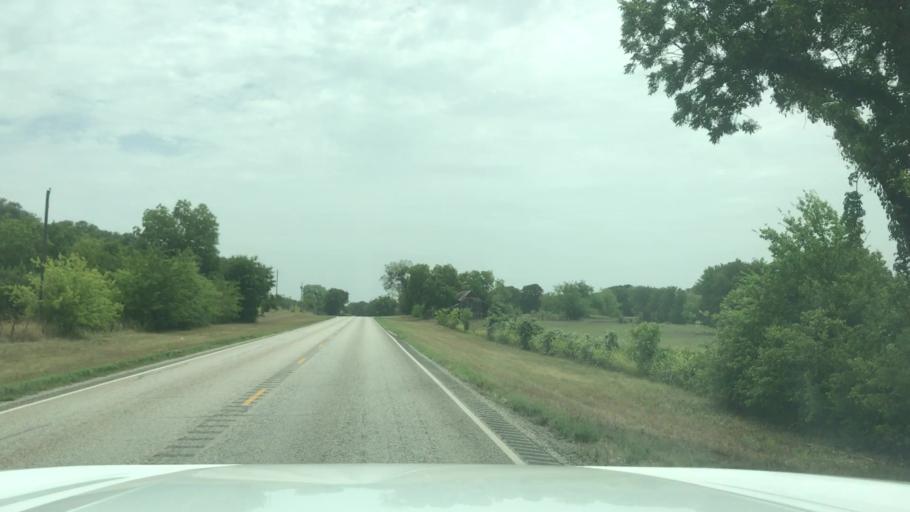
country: US
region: Texas
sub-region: Hamilton County
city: Hico
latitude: 32.0411
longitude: -98.1286
